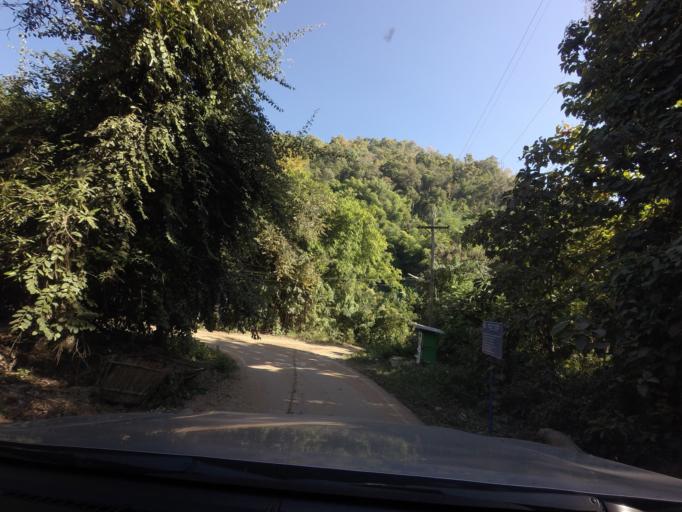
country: TH
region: Lampang
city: Chae Hom
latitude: 18.6146
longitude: 99.6742
